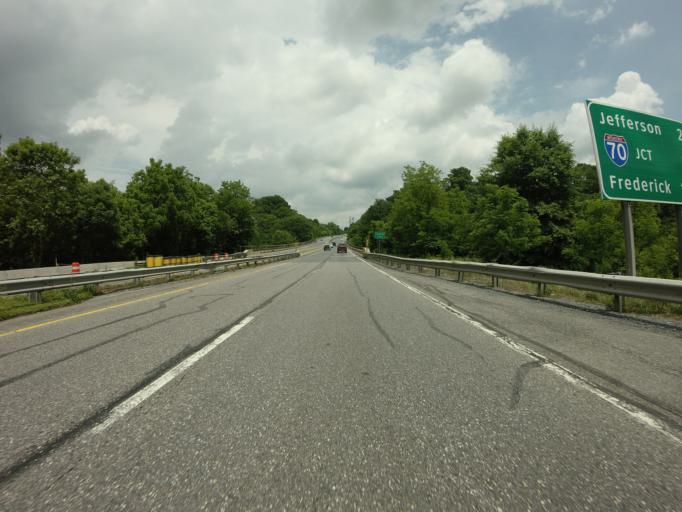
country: US
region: Maryland
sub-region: Frederick County
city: Jefferson
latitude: 39.3550
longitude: -77.5726
